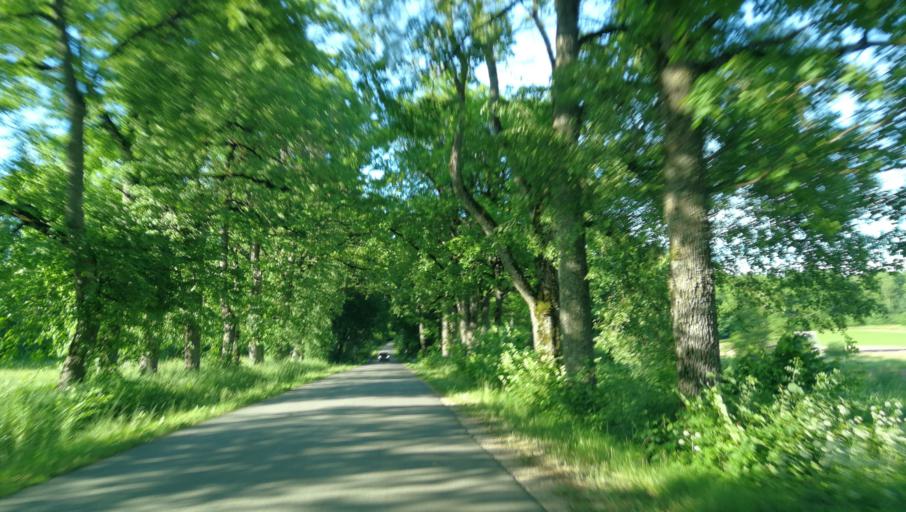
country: LV
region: Pargaujas
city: Stalbe
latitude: 57.3592
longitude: 25.0894
